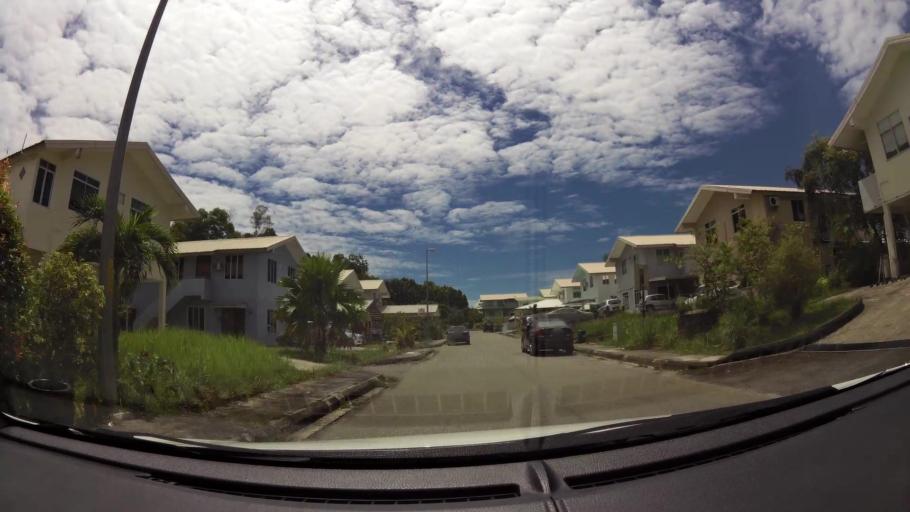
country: BN
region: Brunei and Muara
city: Bandar Seri Begawan
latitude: 4.9930
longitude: 115.0069
